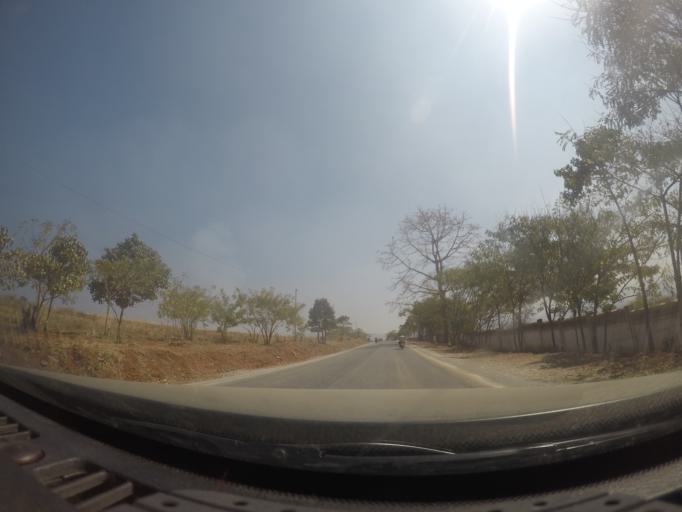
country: MM
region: Shan
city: Taunggyi
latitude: 20.8061
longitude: 97.1965
